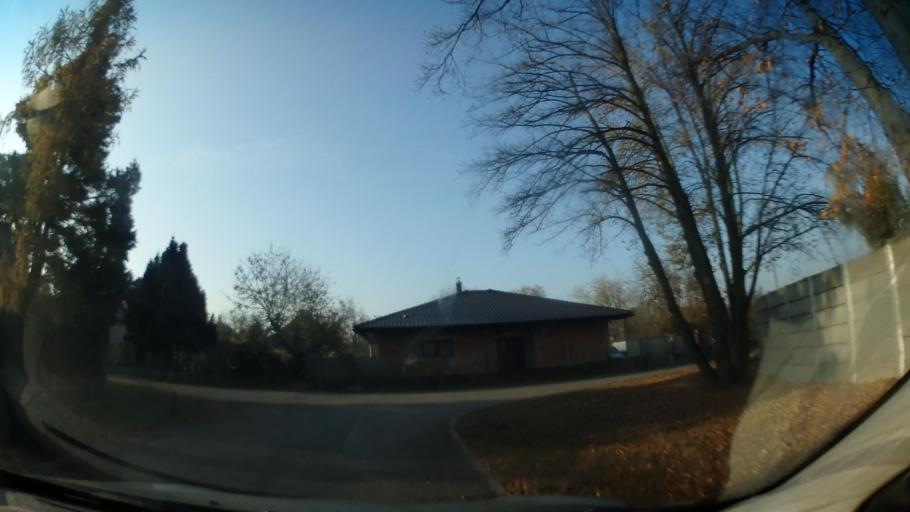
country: CZ
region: Central Bohemia
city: Jirny
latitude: 50.1068
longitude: 14.7077
